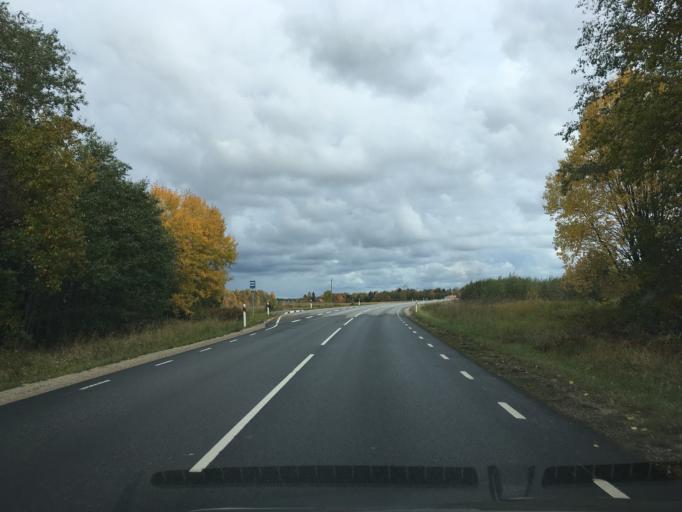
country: EE
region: Harju
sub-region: Anija vald
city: Kehra
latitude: 59.2728
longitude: 25.3578
